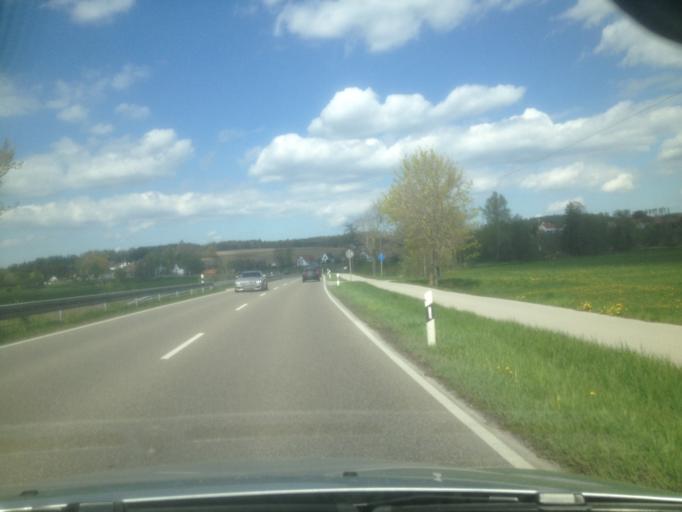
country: DE
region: Bavaria
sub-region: Swabia
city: Diedorf
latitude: 48.3704
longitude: 10.7914
